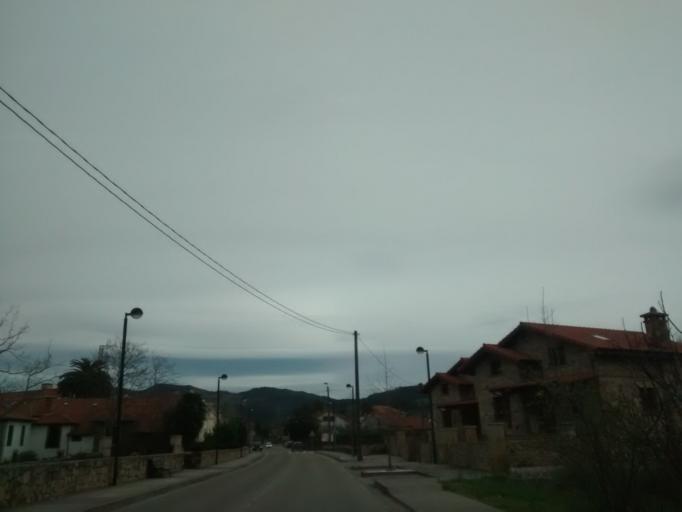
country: ES
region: Cantabria
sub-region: Provincia de Cantabria
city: Puente Viesgo
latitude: 43.3178
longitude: -3.9551
